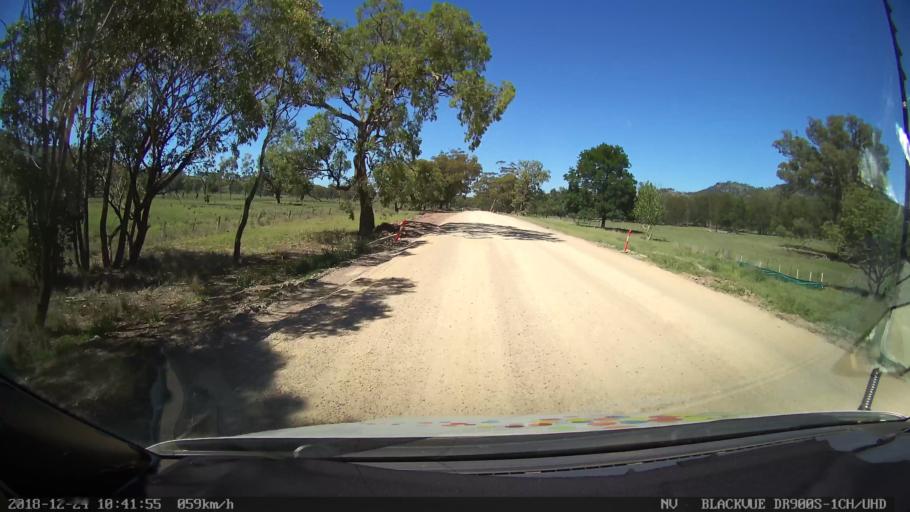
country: AU
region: New South Wales
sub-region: Upper Hunter Shire
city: Merriwa
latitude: -31.8726
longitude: 150.4562
